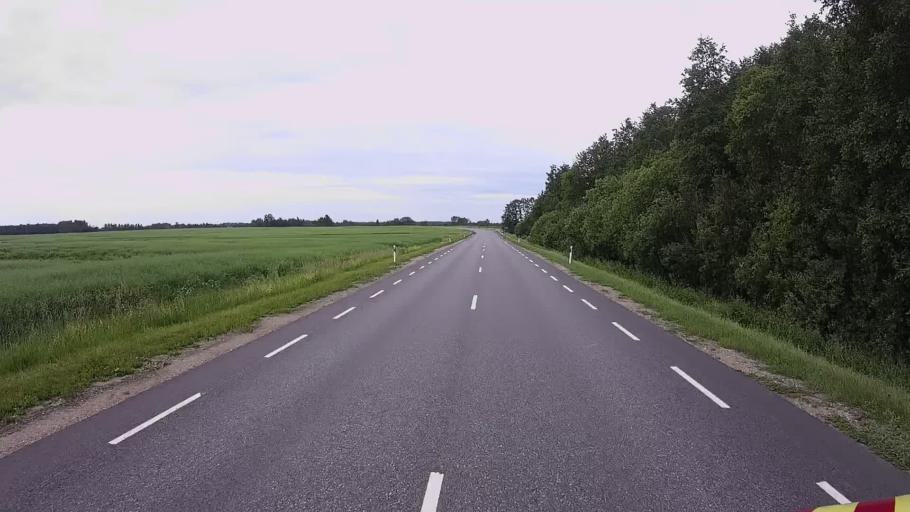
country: EE
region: Viljandimaa
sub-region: Karksi vald
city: Karksi-Nuia
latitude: 58.1737
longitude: 25.5824
